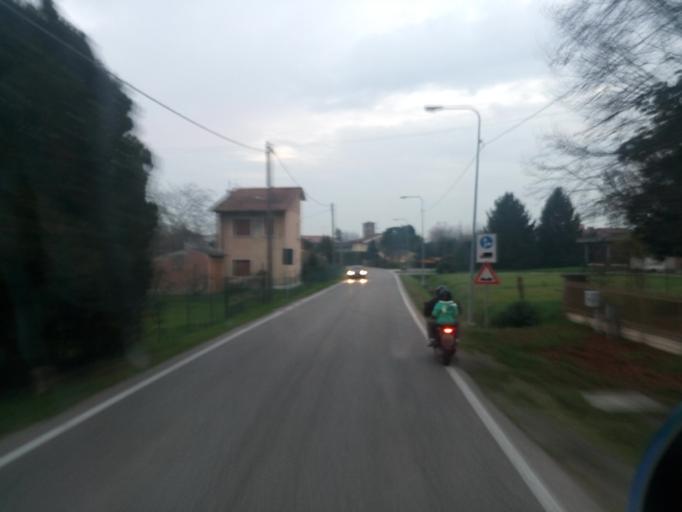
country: IT
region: Lombardy
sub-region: Provincia di Mantova
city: Roncoferraro
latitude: 45.1405
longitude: 10.9388
